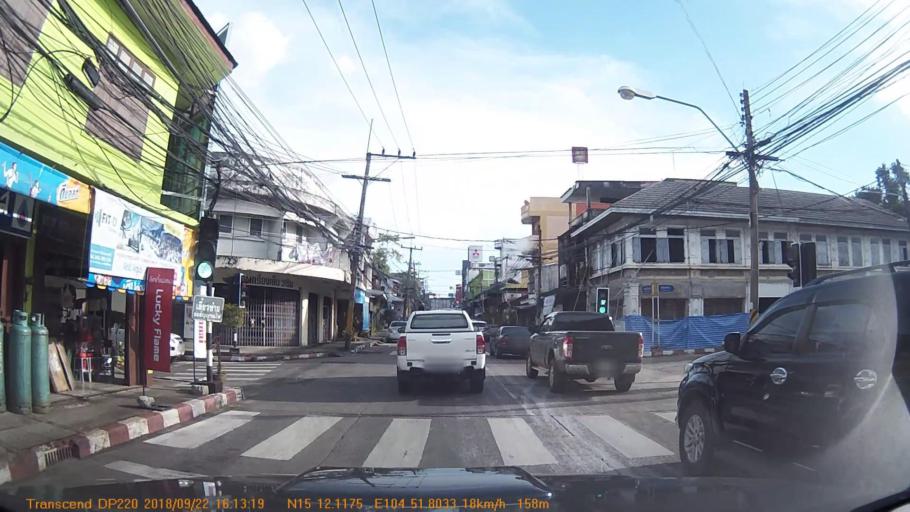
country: TH
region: Changwat Ubon Ratchathani
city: Warin Chamrap
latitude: 15.2020
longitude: 104.8635
